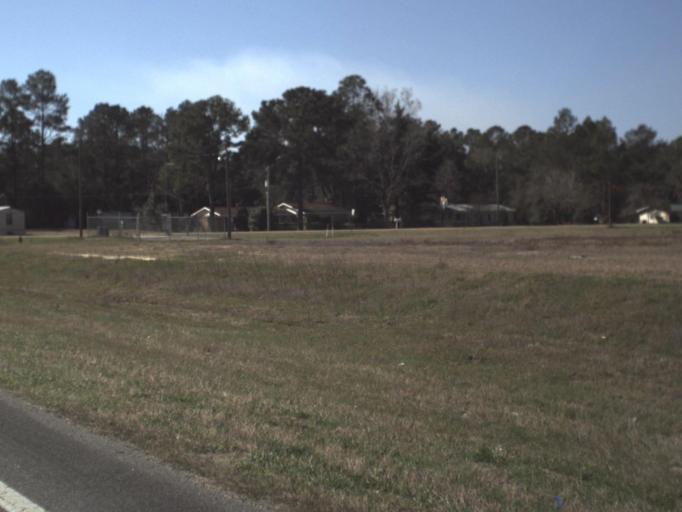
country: US
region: Florida
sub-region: Jackson County
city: Marianna
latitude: 30.7112
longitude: -85.1853
